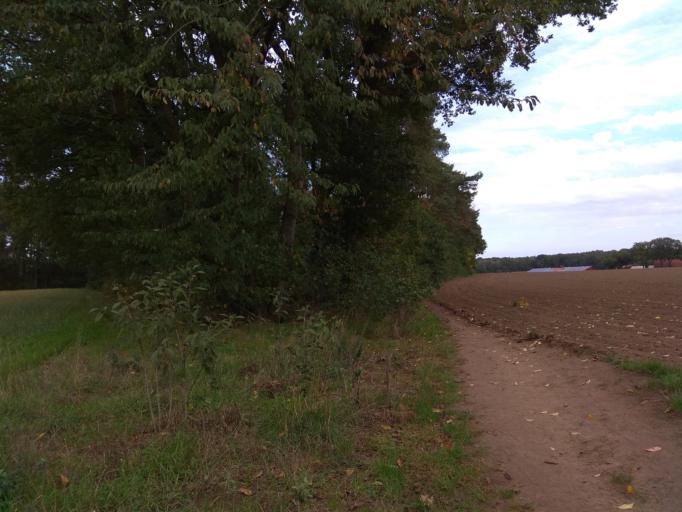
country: DE
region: North Rhine-Westphalia
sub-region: Regierungsbezirk Munster
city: Klein Reken
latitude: 51.7396
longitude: 7.0438
